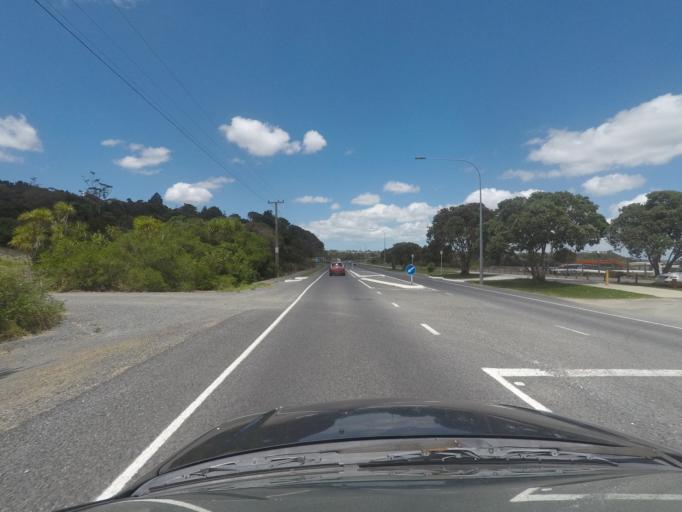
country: NZ
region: Northland
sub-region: Whangarei
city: Whangarei
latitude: -35.7346
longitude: 174.3498
